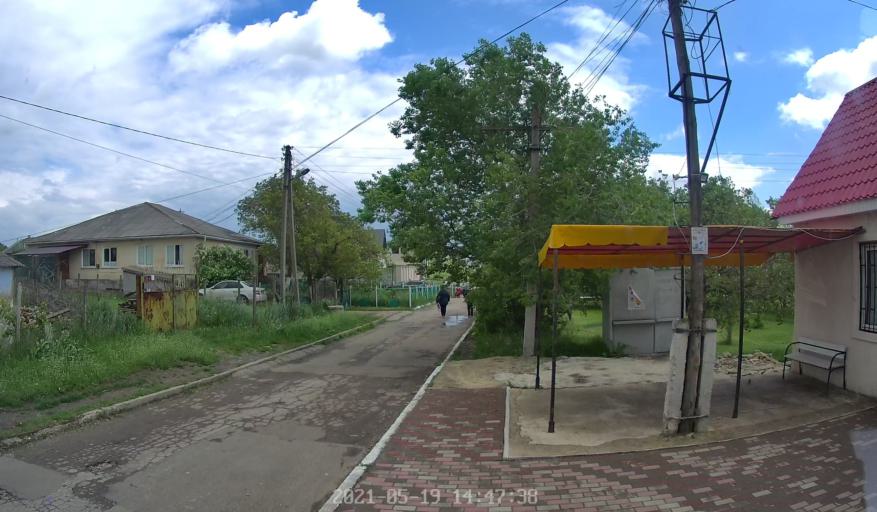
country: MD
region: Chisinau
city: Stauceni
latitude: 47.0445
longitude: 28.9593
